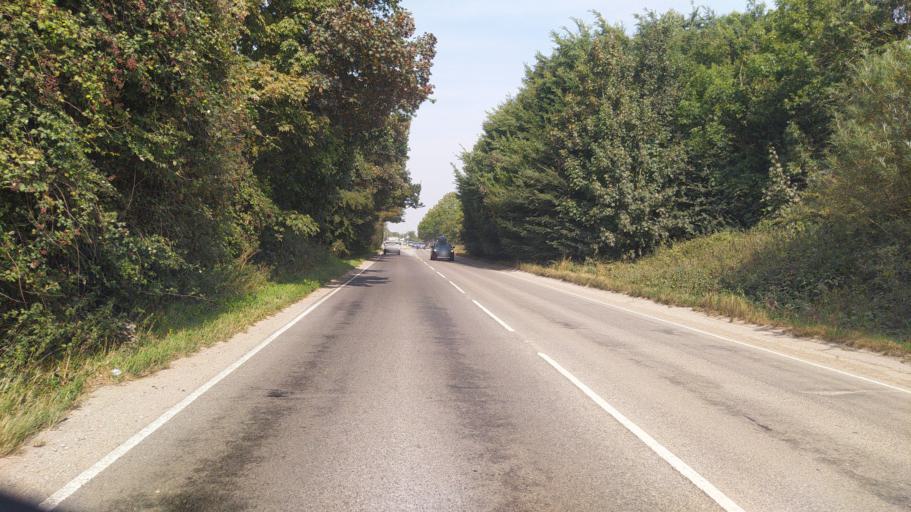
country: GB
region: England
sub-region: West Sussex
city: Bognor Regis
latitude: 50.8093
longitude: -0.7039
